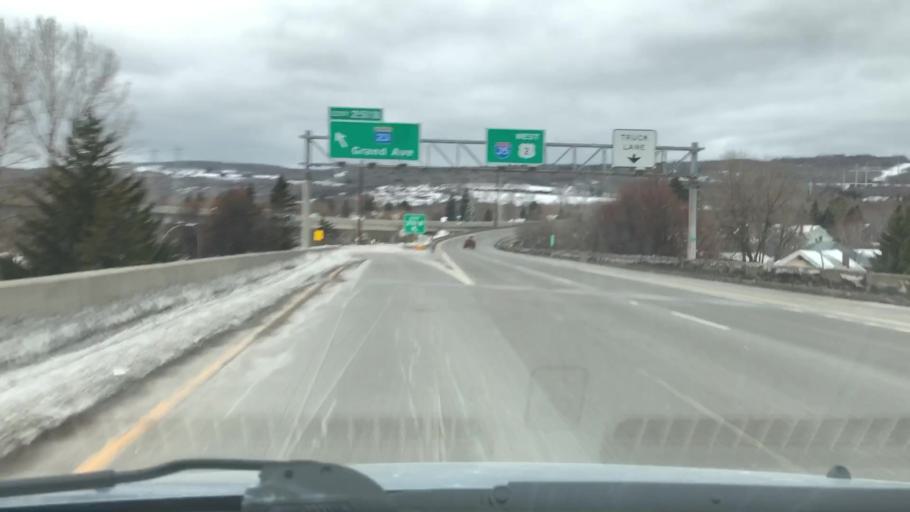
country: US
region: Minnesota
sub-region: Saint Louis County
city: Proctor
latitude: 46.7363
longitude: -92.1722
